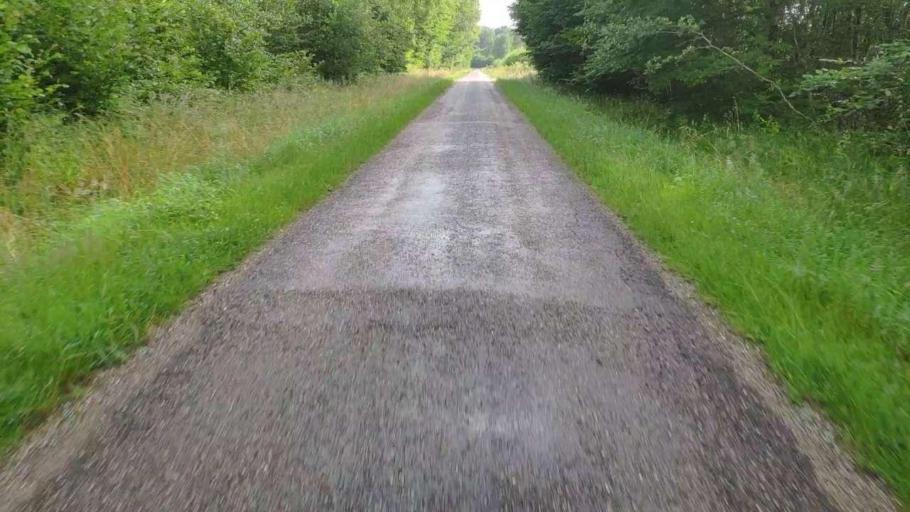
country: FR
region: Franche-Comte
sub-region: Departement du Jura
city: Mont-sous-Vaudrey
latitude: 46.8834
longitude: 5.5245
